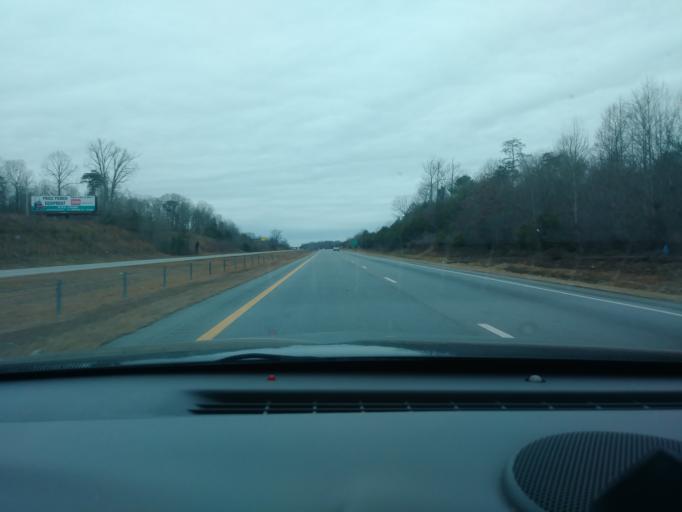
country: US
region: North Carolina
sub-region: Yadkin County
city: Yadkinville
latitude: 36.1198
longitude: -80.6865
